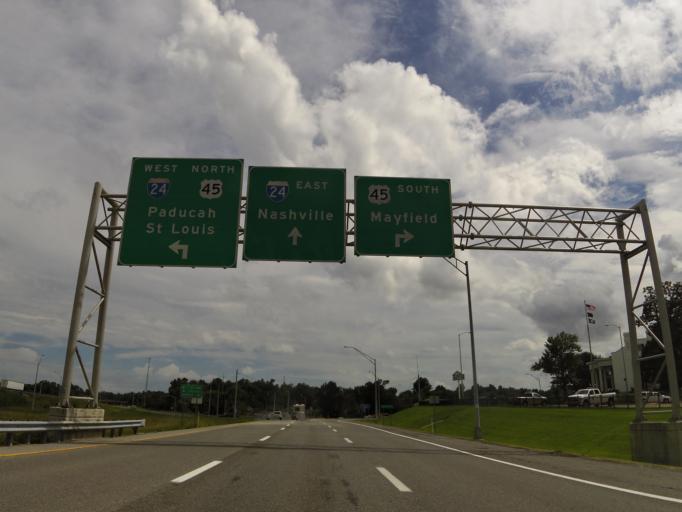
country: US
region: Kentucky
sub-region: McCracken County
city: Hendron
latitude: 37.0520
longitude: -88.6524
